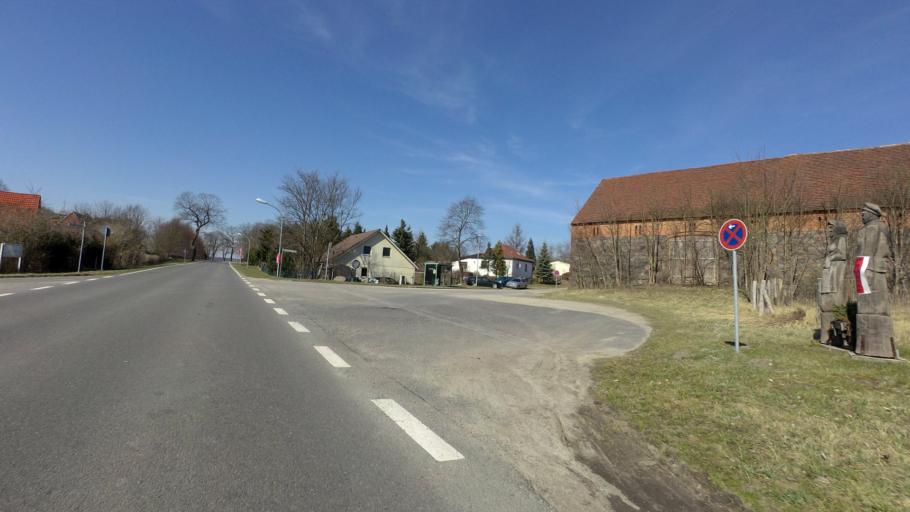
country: DE
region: Brandenburg
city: Protzel
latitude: 52.6304
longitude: 14.0130
